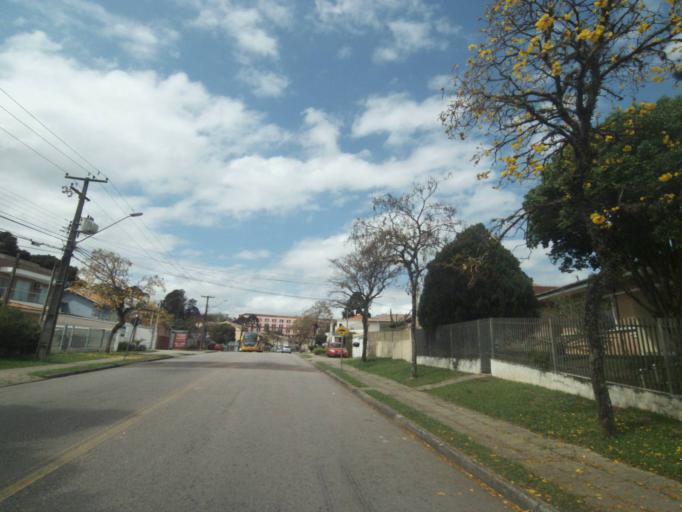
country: BR
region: Parana
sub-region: Pinhais
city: Pinhais
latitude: -25.4136
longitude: -49.2173
